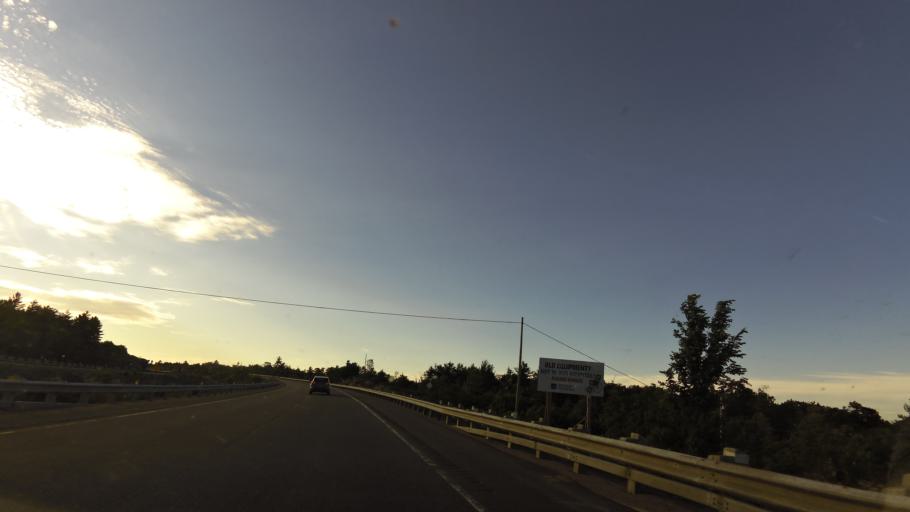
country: CA
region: Ontario
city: Midland
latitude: 44.8907
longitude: -79.7559
